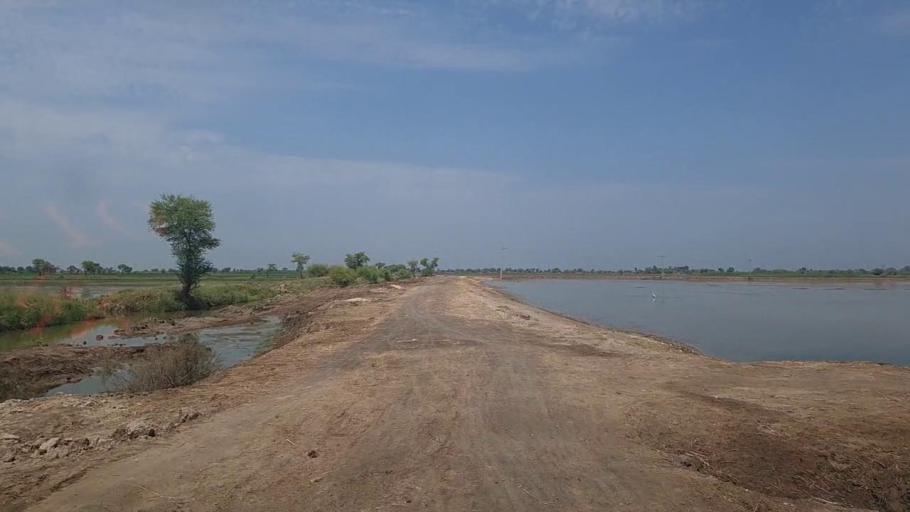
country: PK
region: Sindh
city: Thul
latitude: 28.2991
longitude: 68.6784
